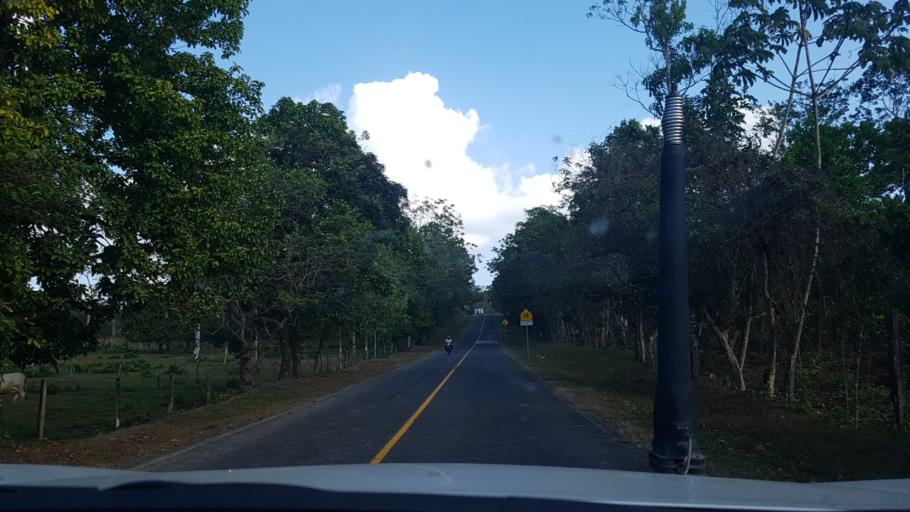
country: NI
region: Atlantico Sur
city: Nueva Guinea
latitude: 11.6948
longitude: -84.4055
